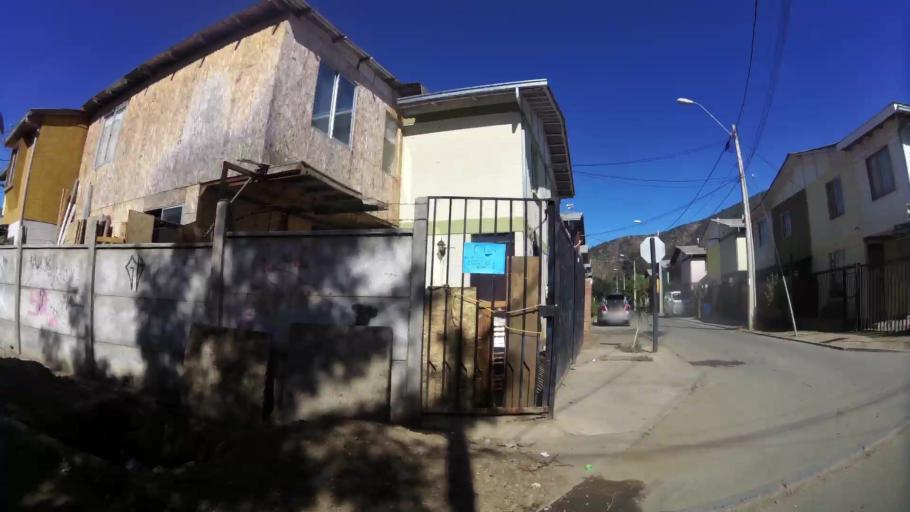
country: CL
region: Santiago Metropolitan
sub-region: Provincia de Chacabuco
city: Lampa
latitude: -33.4063
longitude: -71.1293
